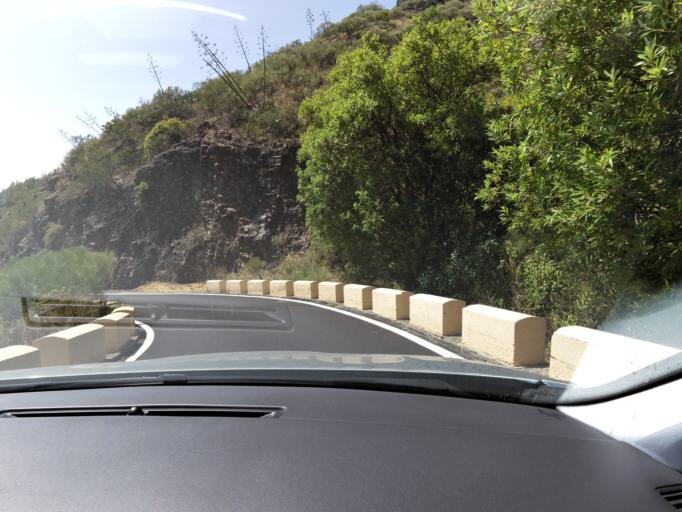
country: ES
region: Canary Islands
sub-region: Provincia de Santa Cruz de Tenerife
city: Santiago del Teide
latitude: 28.3018
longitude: -16.8267
